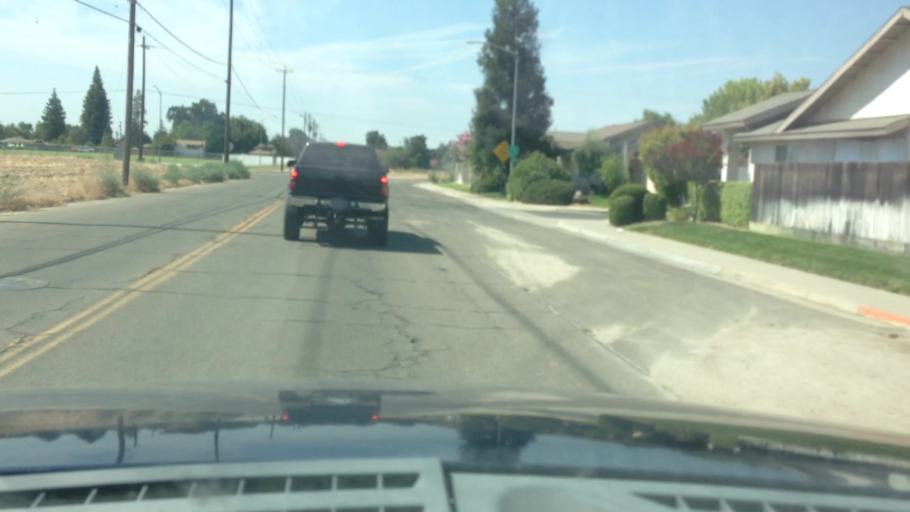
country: US
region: California
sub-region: Fresno County
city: Kingsburg
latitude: 36.5260
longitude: -119.5569
